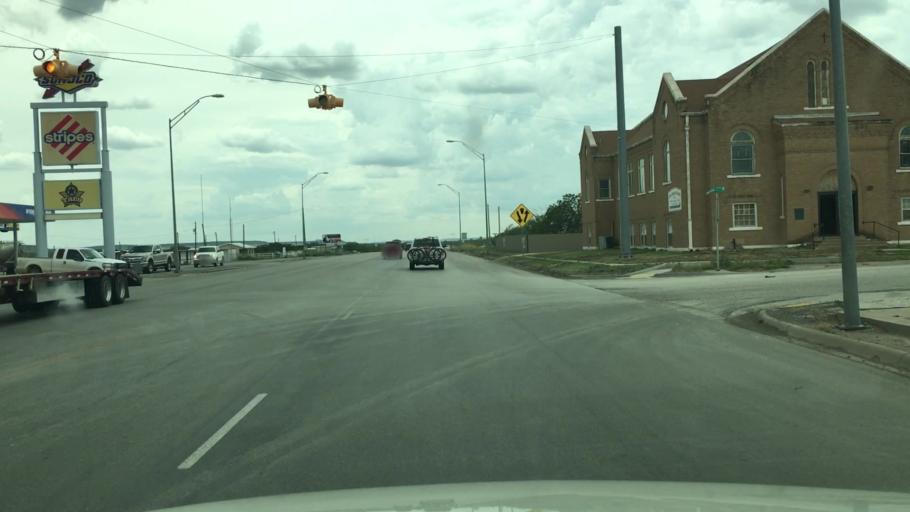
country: US
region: Texas
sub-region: Sterling County
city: Sterling City
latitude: 31.8367
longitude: -100.9937
